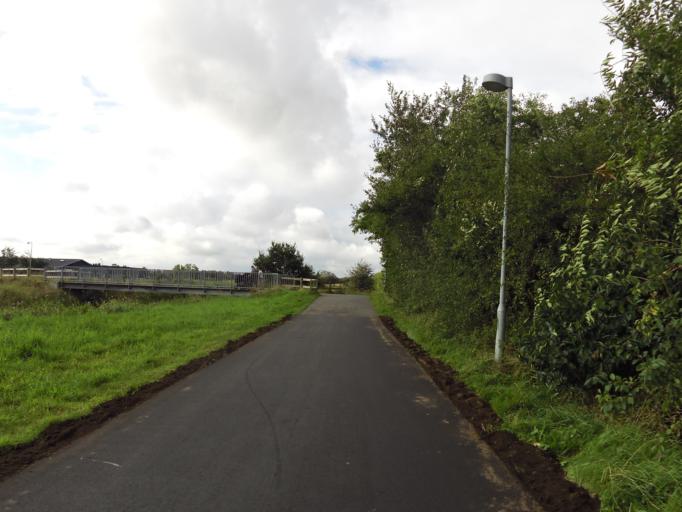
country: DK
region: South Denmark
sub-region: Esbjerg Kommune
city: Ribe
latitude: 55.3346
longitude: 8.7795
